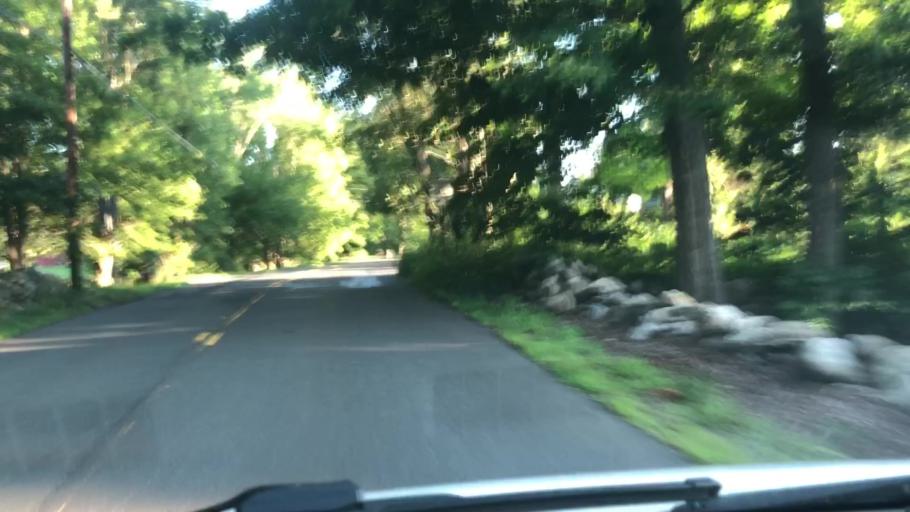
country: US
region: Massachusetts
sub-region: Hampshire County
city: Williamsburg
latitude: 42.3648
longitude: -72.7236
